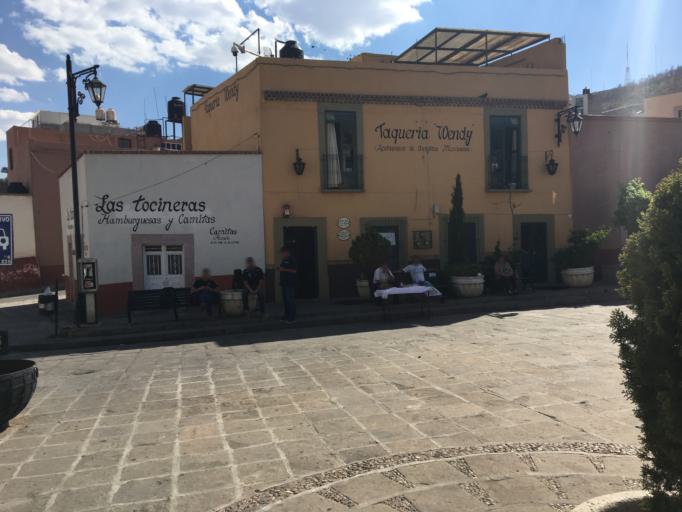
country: MX
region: Zacatecas
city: Zacatecas
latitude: 22.7822
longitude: -102.5711
